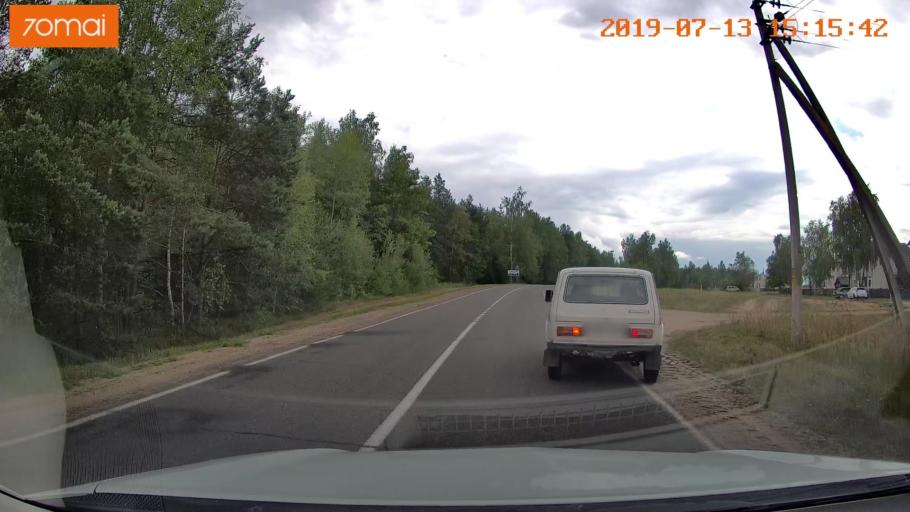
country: BY
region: Mogilev
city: Hlusha
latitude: 53.1150
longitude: 28.8286
